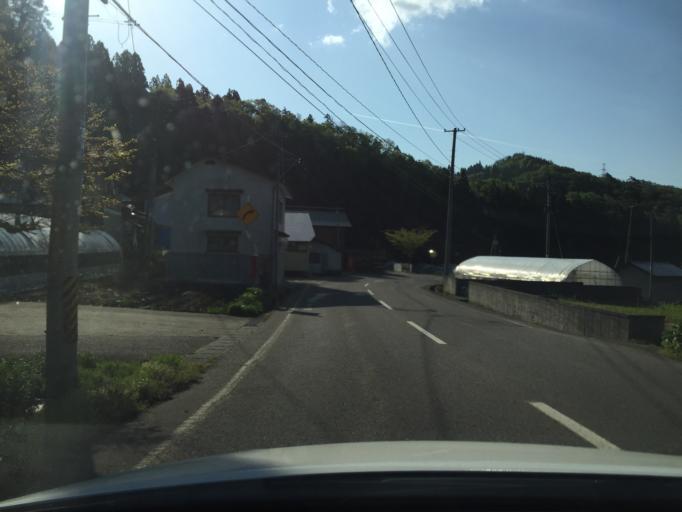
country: JP
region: Fukushima
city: Kitakata
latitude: 37.6715
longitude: 139.7837
